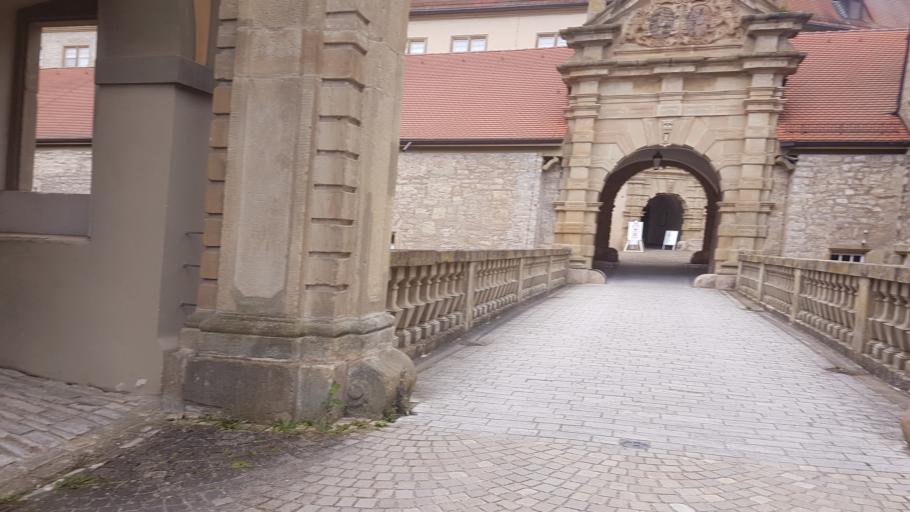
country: DE
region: Baden-Wuerttemberg
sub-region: Regierungsbezirk Stuttgart
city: Weikersheim
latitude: 49.4807
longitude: 9.8969
